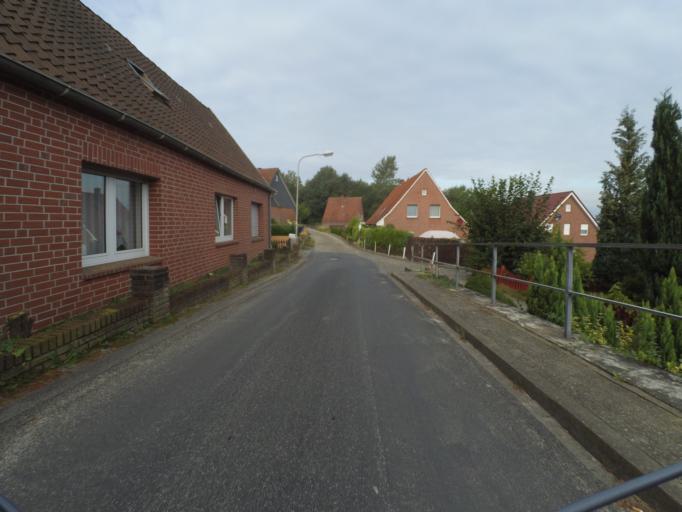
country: DE
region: Lower Saxony
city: Bad Bentheim
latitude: 52.3031
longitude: 7.1055
